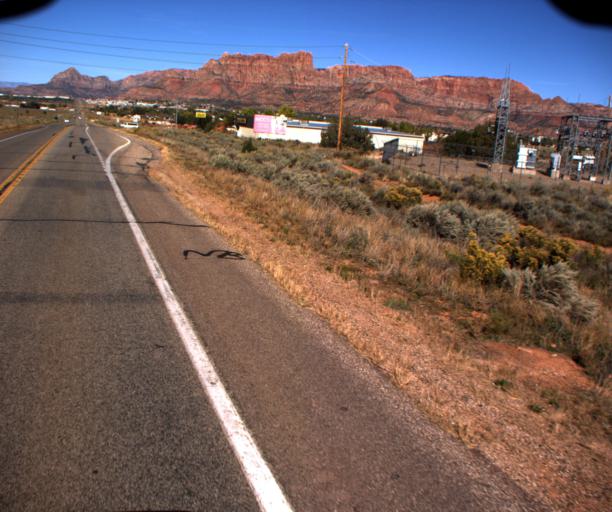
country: US
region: Arizona
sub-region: Mohave County
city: Colorado City
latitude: 36.9698
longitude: -112.9744
